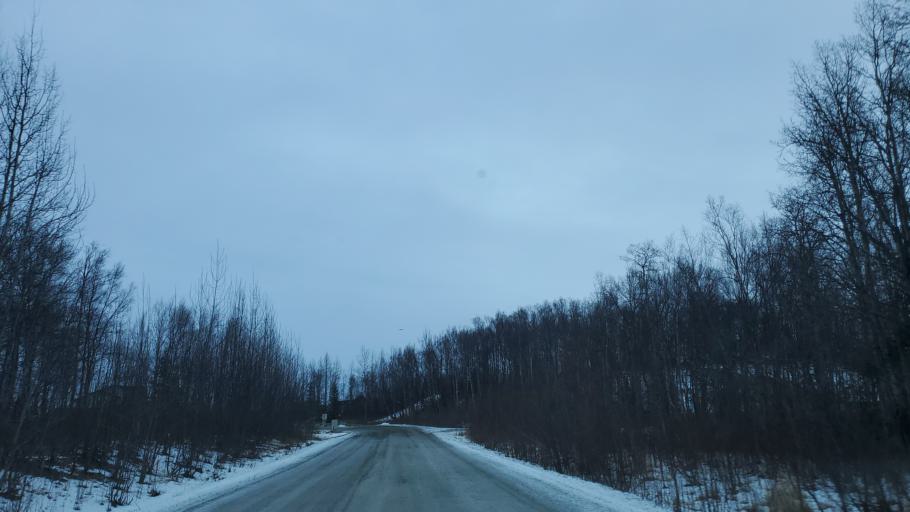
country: US
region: Alaska
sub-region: Matanuska-Susitna Borough
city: Farm Loop
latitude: 61.6524
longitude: -149.2190
